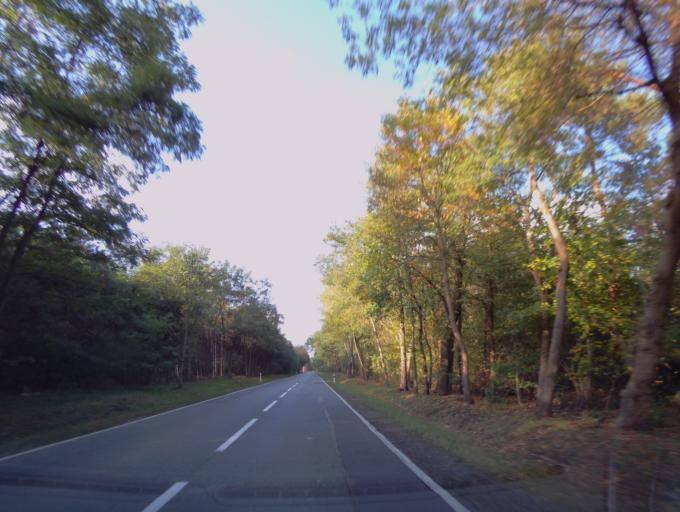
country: PL
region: Subcarpathian Voivodeship
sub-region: Powiat nizanski
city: Krzeszow
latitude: 50.3772
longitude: 22.3113
